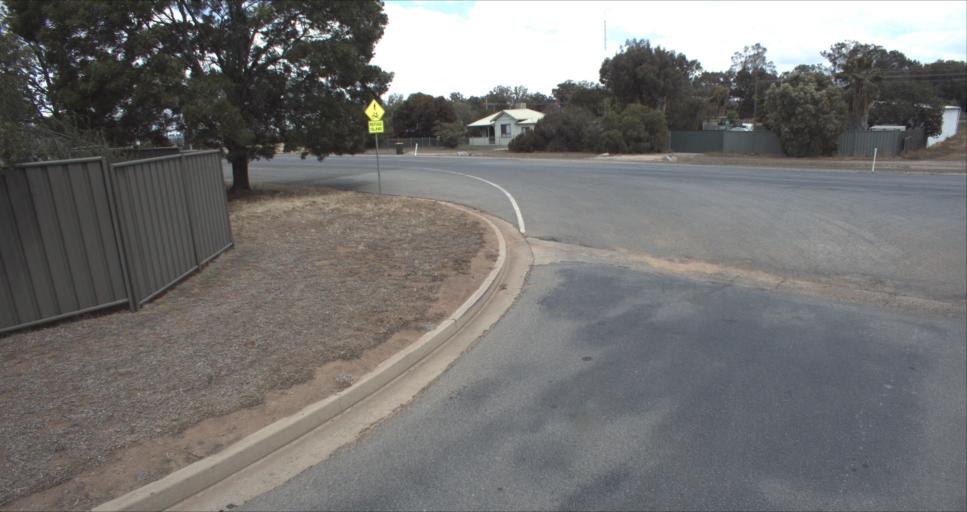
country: AU
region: New South Wales
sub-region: Leeton
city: Leeton
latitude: -34.5609
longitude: 146.3927
